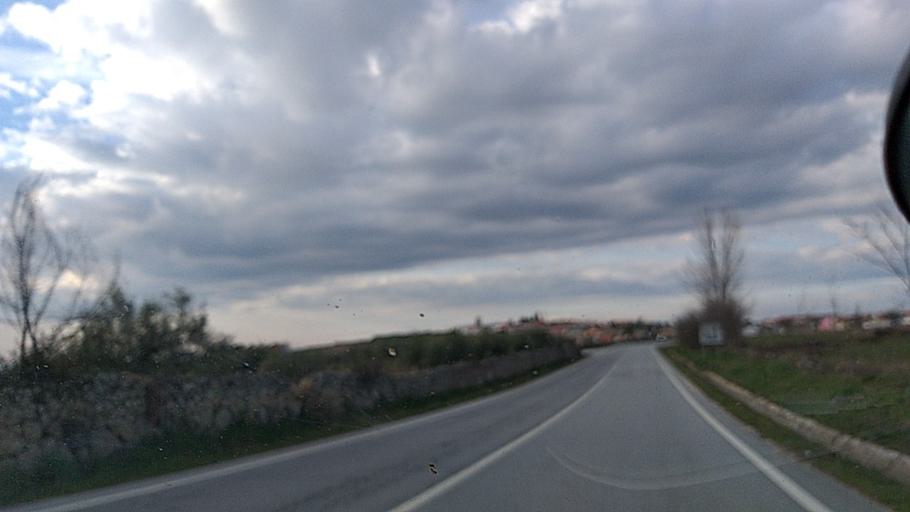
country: ES
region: Castille and Leon
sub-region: Provincia de Salamanca
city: Aldea del Obispo
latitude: 40.7155
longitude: -6.9009
